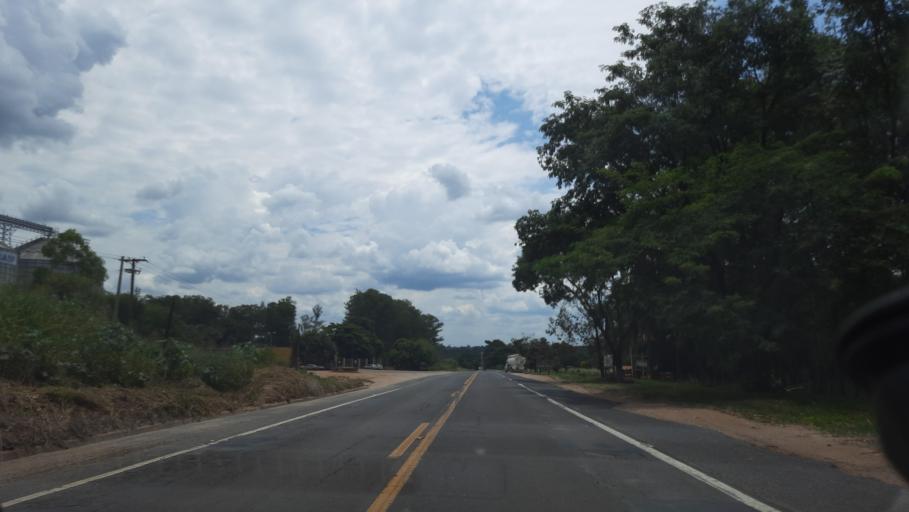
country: BR
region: Sao Paulo
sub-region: Mococa
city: Mococa
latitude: -21.5072
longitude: -47.0489
